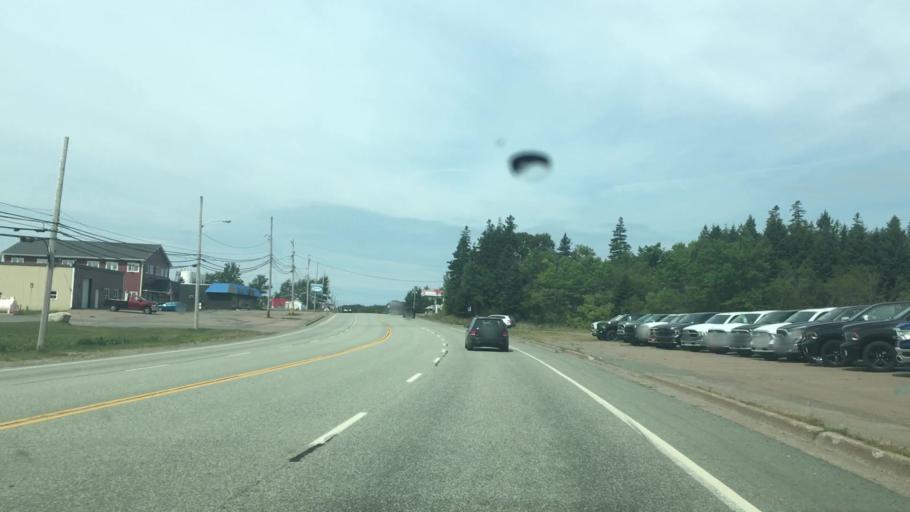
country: CA
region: Nova Scotia
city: Port Hawkesbury
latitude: 45.6393
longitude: -61.3849
